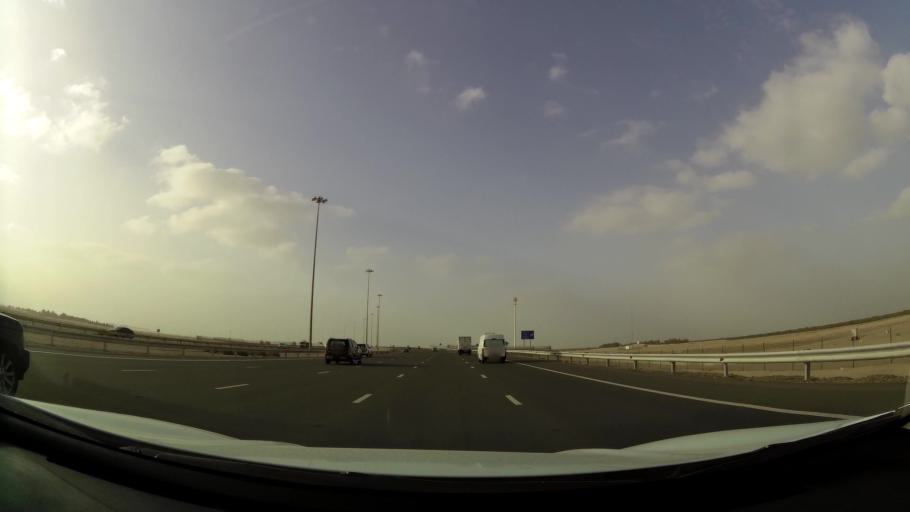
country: AE
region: Abu Dhabi
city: Abu Dhabi
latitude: 24.5391
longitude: 54.4846
